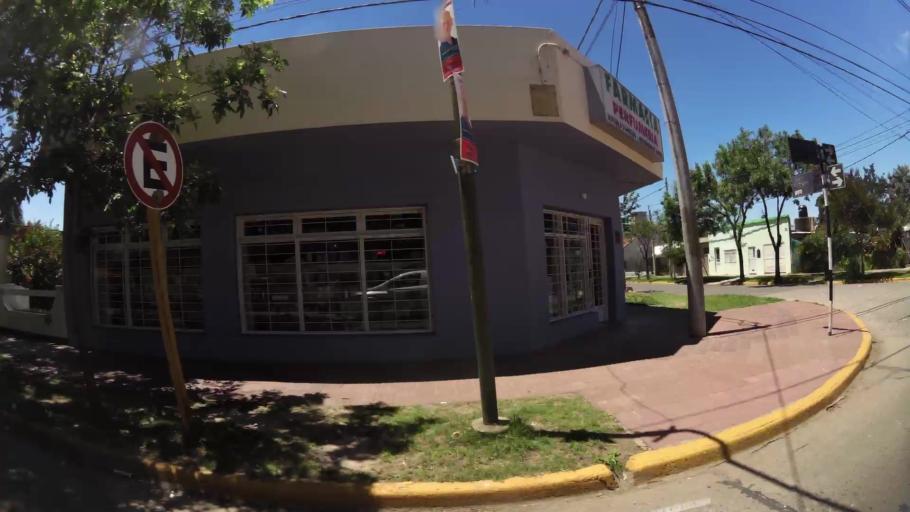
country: AR
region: Santa Fe
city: Rafaela
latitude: -31.2516
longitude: -61.4633
